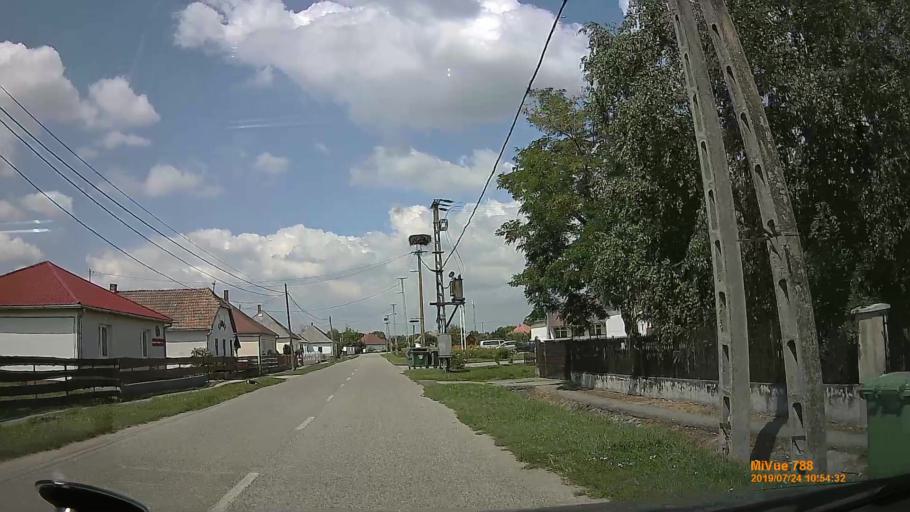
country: HU
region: Szabolcs-Szatmar-Bereg
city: Tarpa
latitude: 48.1973
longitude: 22.5318
